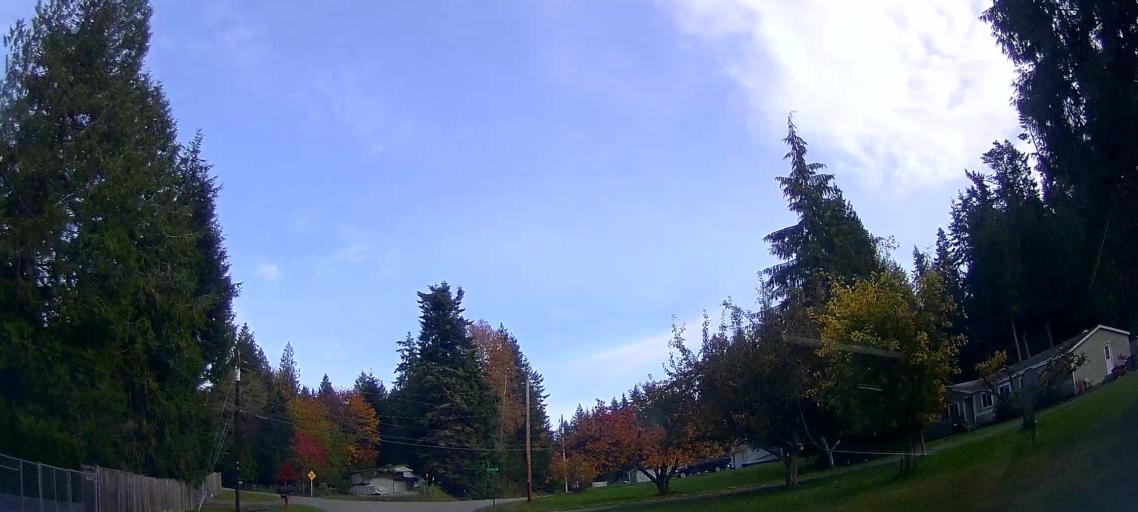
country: US
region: Washington
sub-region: Snohomish County
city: Stanwood
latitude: 48.2802
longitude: -122.3456
